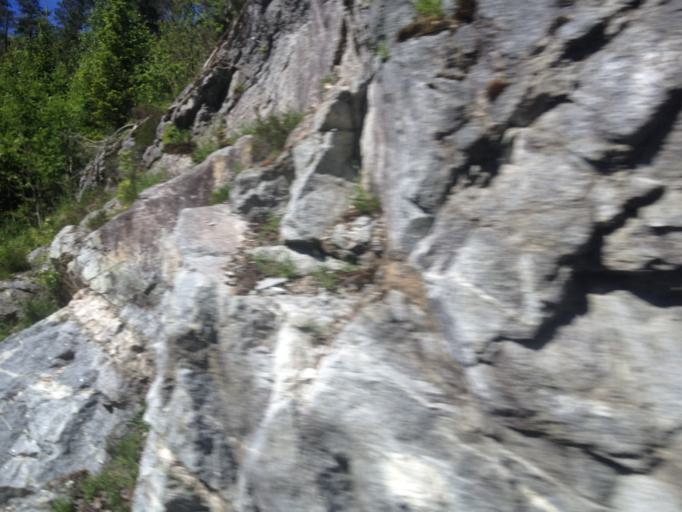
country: NO
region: Rogaland
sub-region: Sokndal
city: Hauge i Dalane
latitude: 58.4691
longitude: 6.3863
